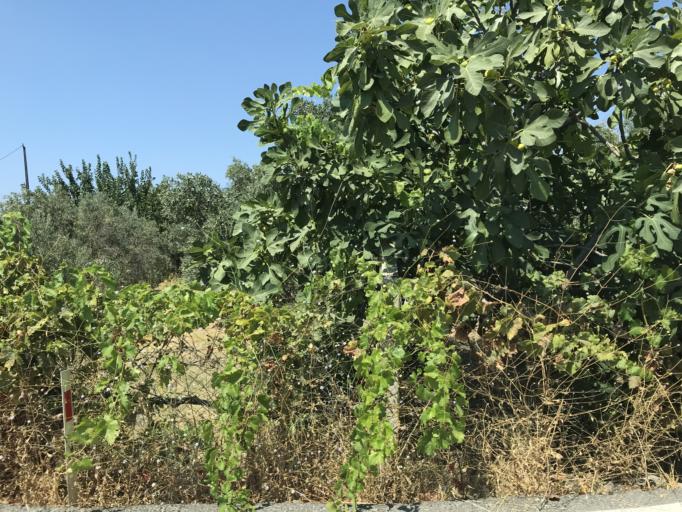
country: TR
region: Izmir
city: Urla
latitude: 38.2823
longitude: 26.7341
